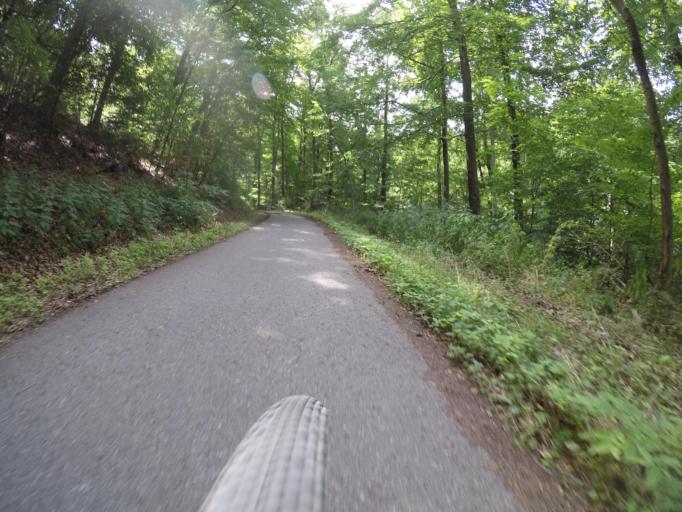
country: DE
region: Baden-Wuerttemberg
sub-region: Regierungsbezirk Stuttgart
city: Magstadt
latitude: 48.7365
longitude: 8.9977
